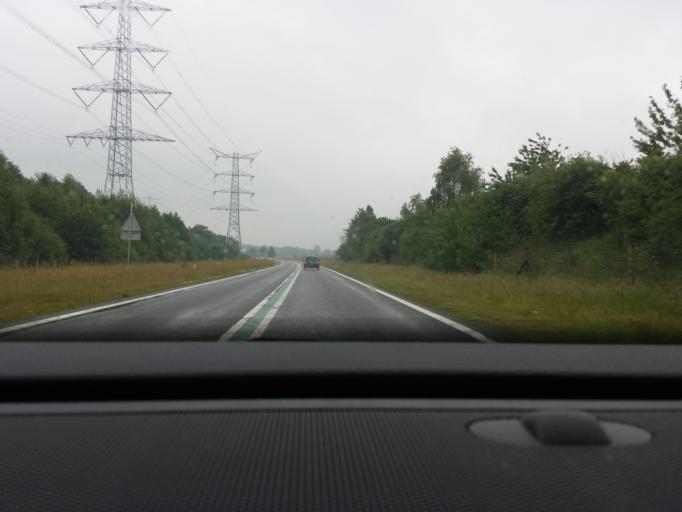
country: NL
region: Overijssel
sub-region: Gemeente Enschede
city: Enschede
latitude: 52.1995
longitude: 6.9345
